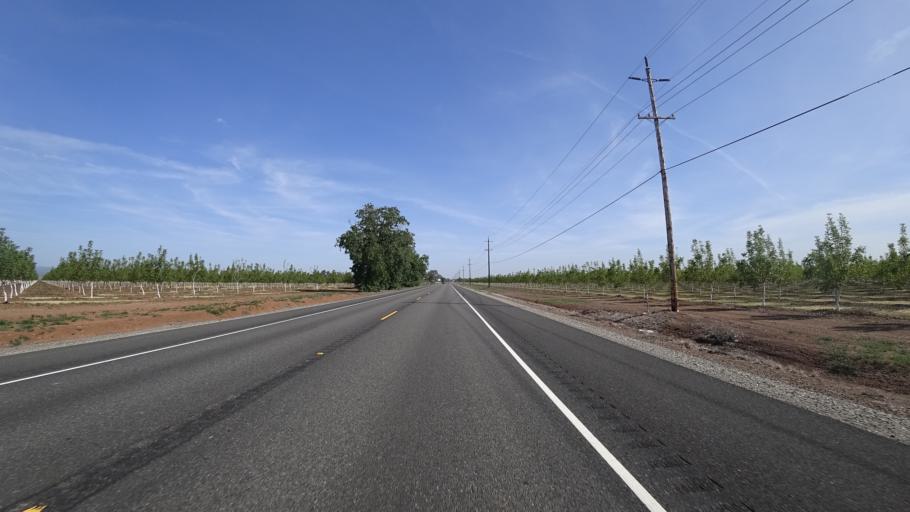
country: US
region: California
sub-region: Glenn County
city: Hamilton City
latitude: 39.8366
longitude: -121.9371
